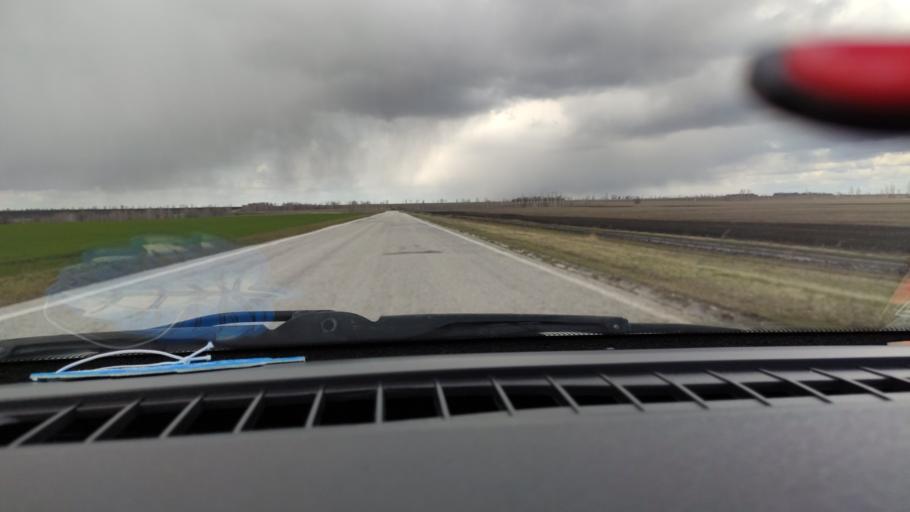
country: RU
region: Samara
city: Povolzhskiy
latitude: 53.7938
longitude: 49.7293
